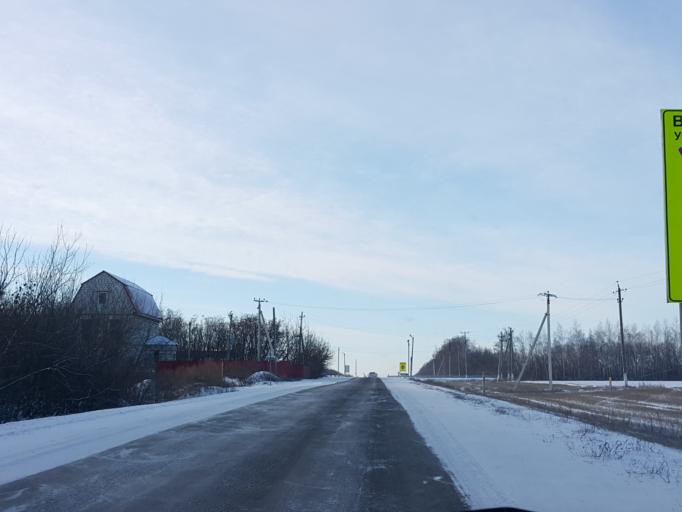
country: RU
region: Tambov
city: Znamenka
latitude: 52.4038
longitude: 41.3938
